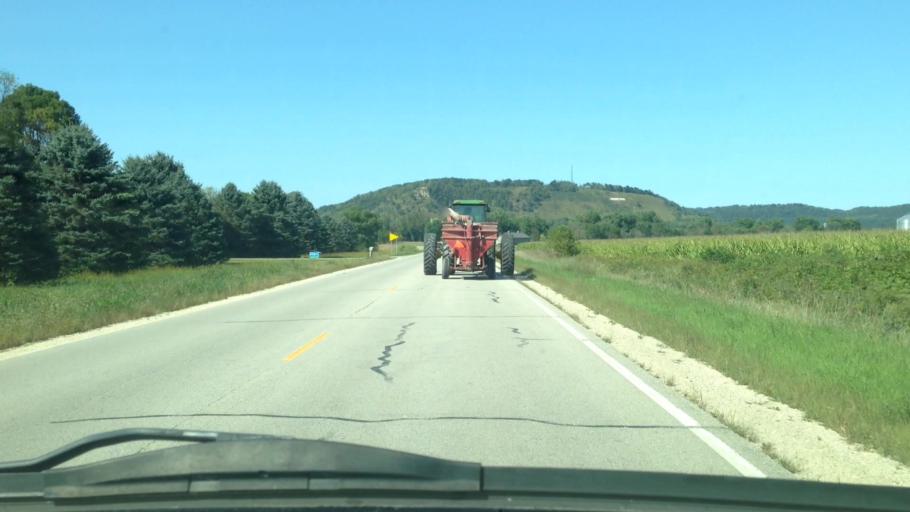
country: US
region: Minnesota
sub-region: Fillmore County
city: Rushford
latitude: 43.7885
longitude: -91.7653
